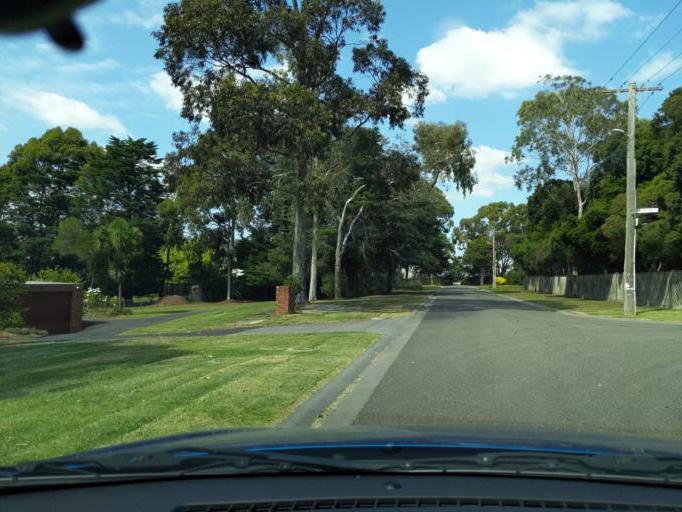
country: AU
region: Victoria
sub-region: Knox
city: Rowville
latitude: -37.9242
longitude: 145.2508
